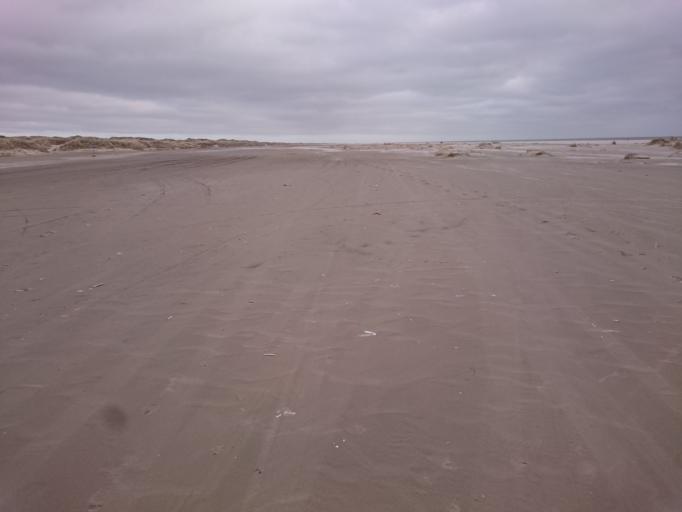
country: DK
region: South Denmark
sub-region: Fano Kommune
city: Nordby
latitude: 55.4163
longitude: 8.3785
